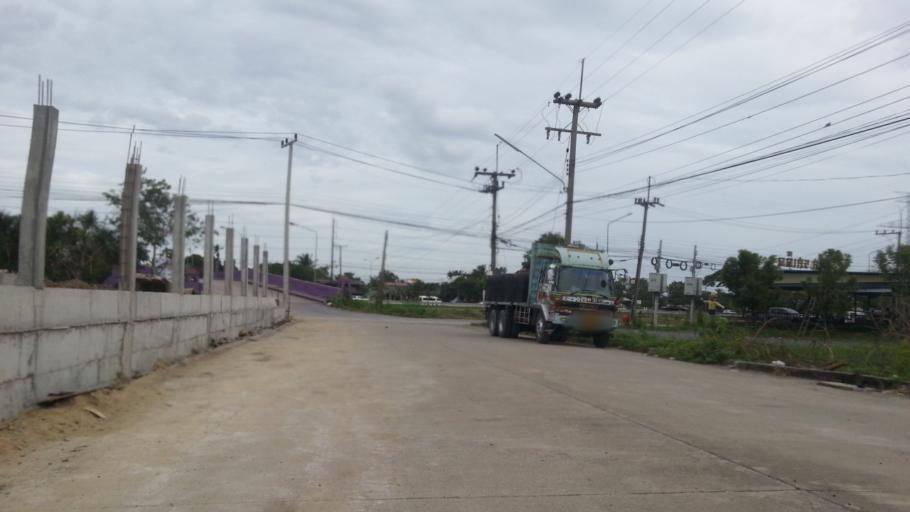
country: TH
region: Pathum Thani
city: Nong Suea
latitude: 14.0705
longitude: 100.8787
